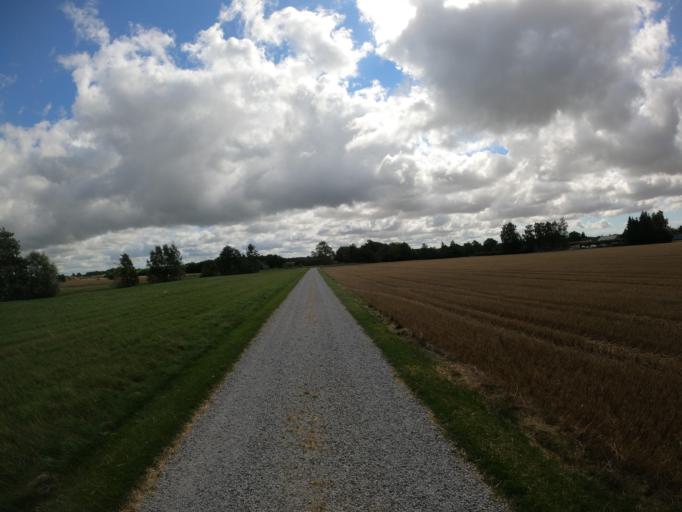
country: SE
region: Skane
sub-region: Eslovs Kommun
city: Eslov
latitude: 55.7274
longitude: 13.3497
